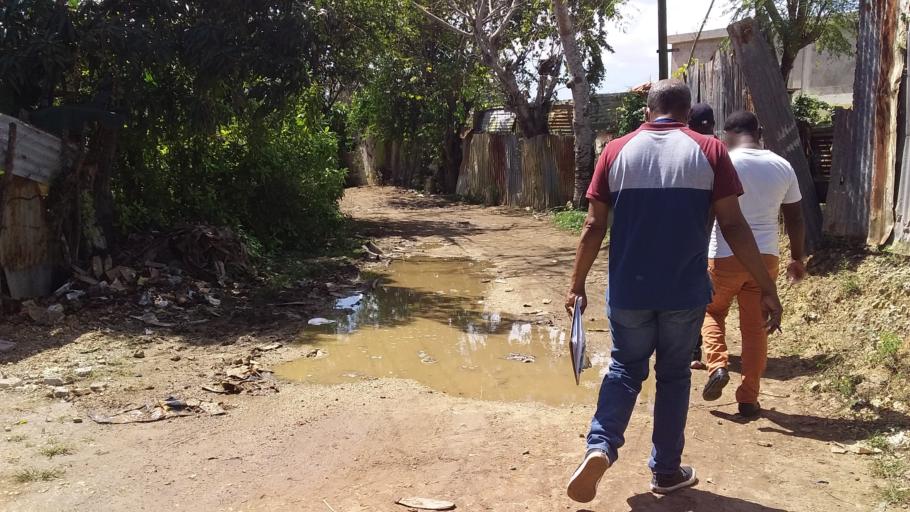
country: DO
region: Santo Domingo
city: Guerra
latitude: 18.5616
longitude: -69.7814
